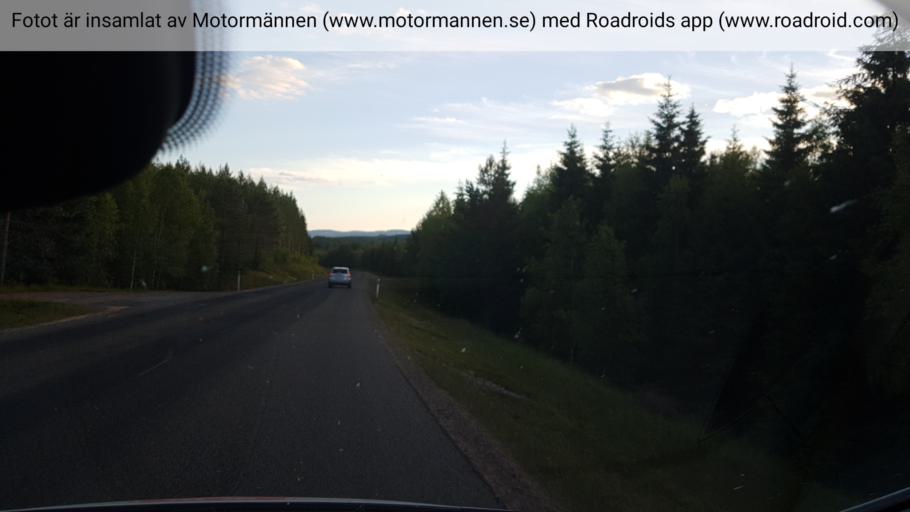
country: SE
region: Vaermland
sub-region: Torsby Kommun
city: Torsby
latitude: 60.3339
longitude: 13.1417
